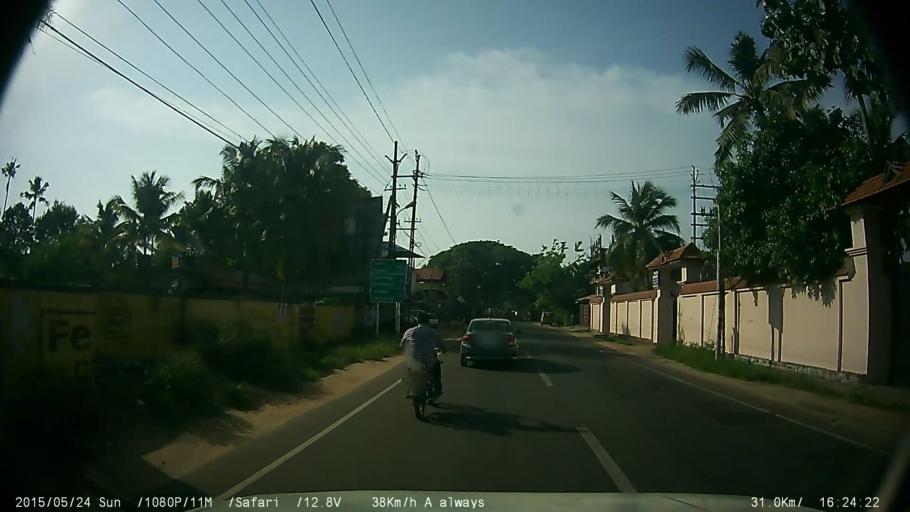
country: IN
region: Kerala
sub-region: Alappuzha
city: Alleppey
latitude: 9.5061
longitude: 76.3283
